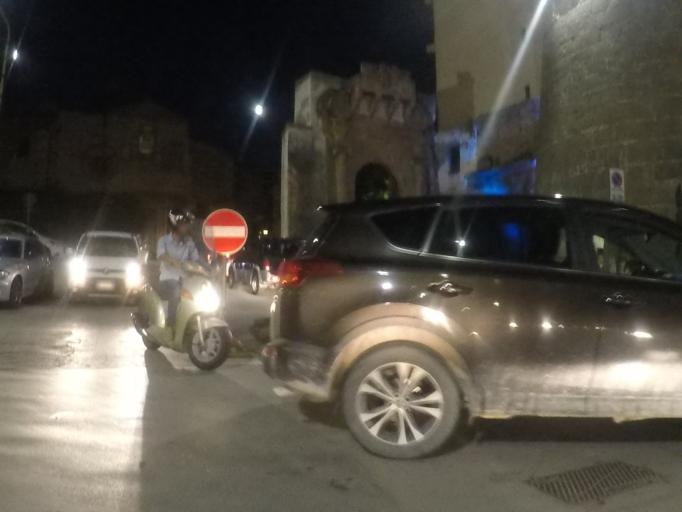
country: IT
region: Sicily
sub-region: Agrigento
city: Sciacca
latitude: 37.5089
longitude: 13.0778
